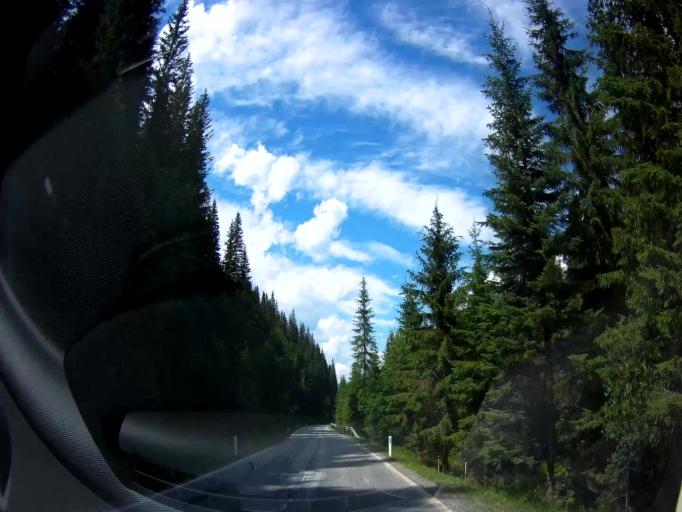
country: AT
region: Styria
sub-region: Politischer Bezirk Murau
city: Stadl an der Mur
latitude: 46.9971
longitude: 14.0150
